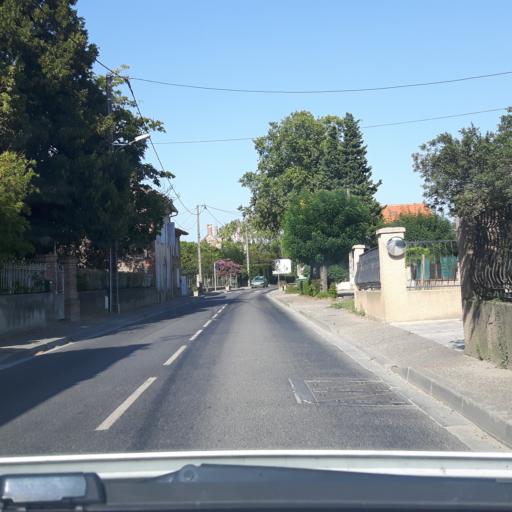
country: FR
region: Midi-Pyrenees
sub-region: Departement de la Haute-Garonne
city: Ondes
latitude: 43.7807
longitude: 1.3118
